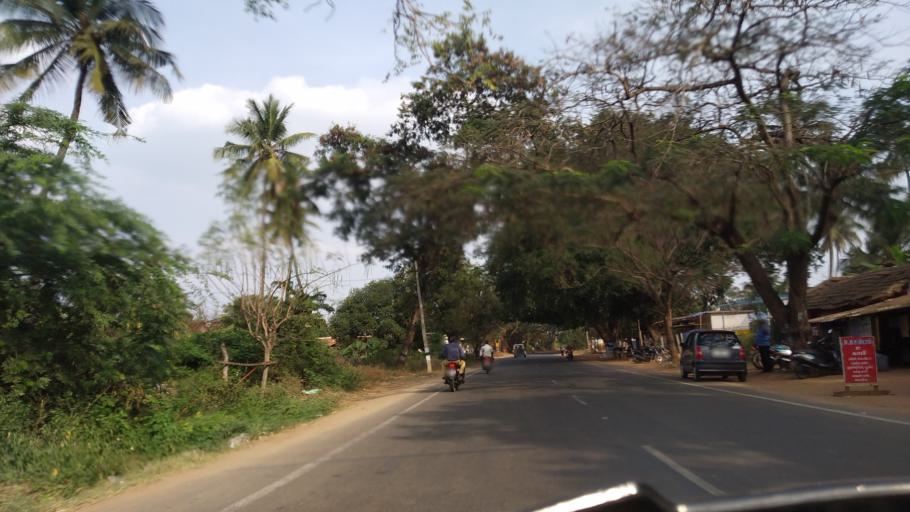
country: IN
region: Tamil Nadu
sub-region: Coimbatore
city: Perur
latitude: 10.9721
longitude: 76.8820
